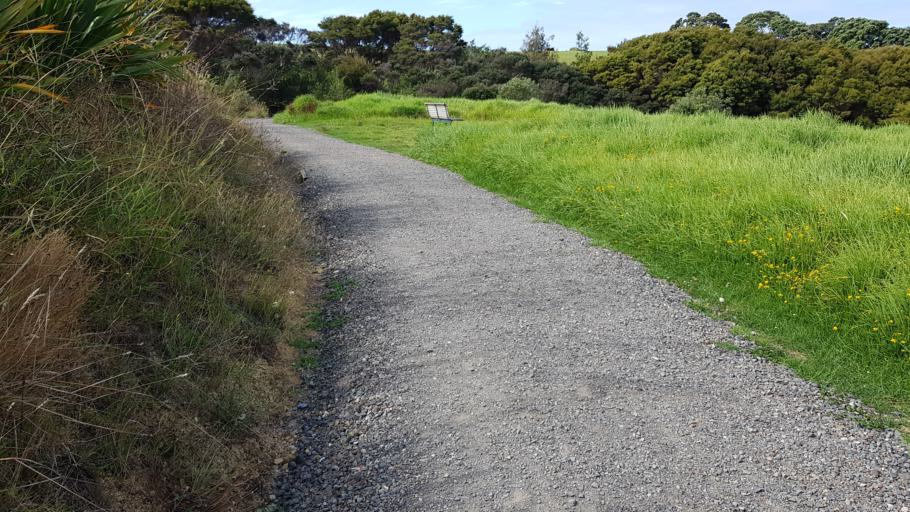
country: NZ
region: Auckland
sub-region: Auckland
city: Rothesay Bay
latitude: -36.6724
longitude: 174.7459
